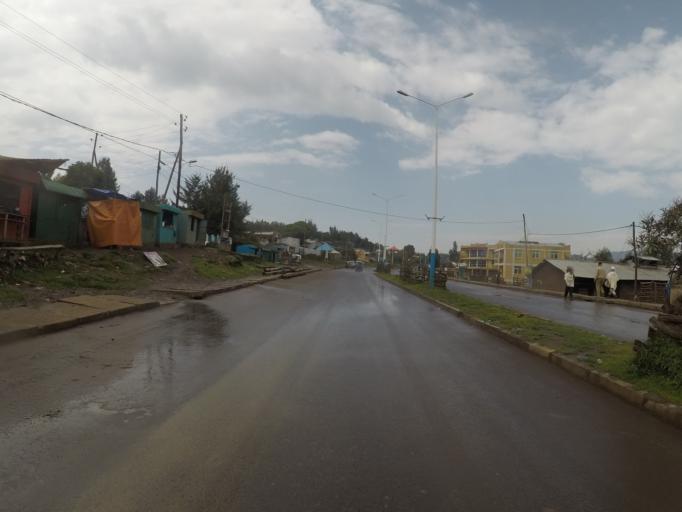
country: ET
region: Amhara
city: Debark'
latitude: 13.1466
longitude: 37.8944
